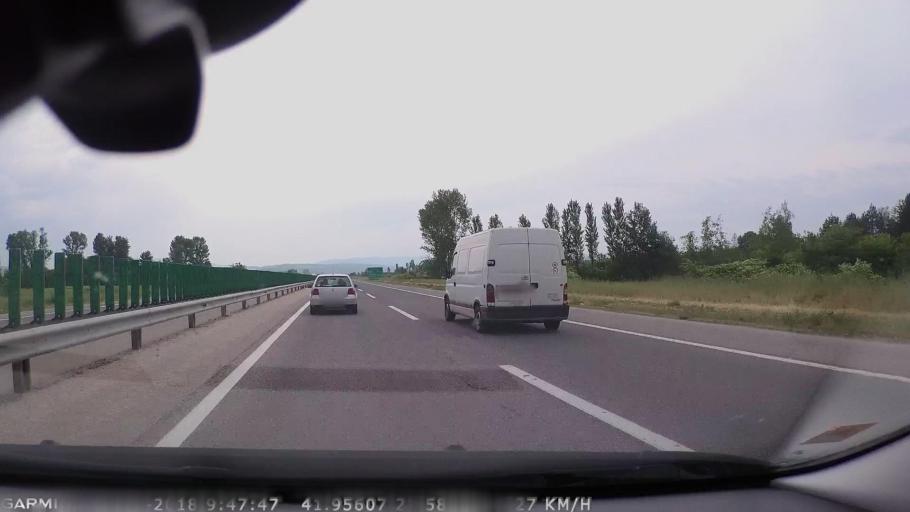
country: MK
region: Ilinden
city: Idrizovo
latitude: 41.9678
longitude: 21.5731
